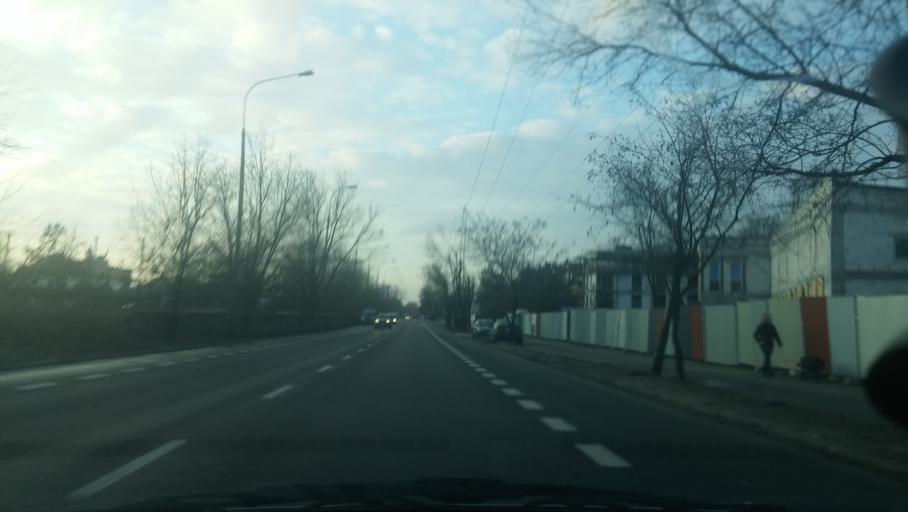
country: PL
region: Masovian Voivodeship
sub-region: Warszawa
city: Wawer
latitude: 52.2110
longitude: 21.1625
